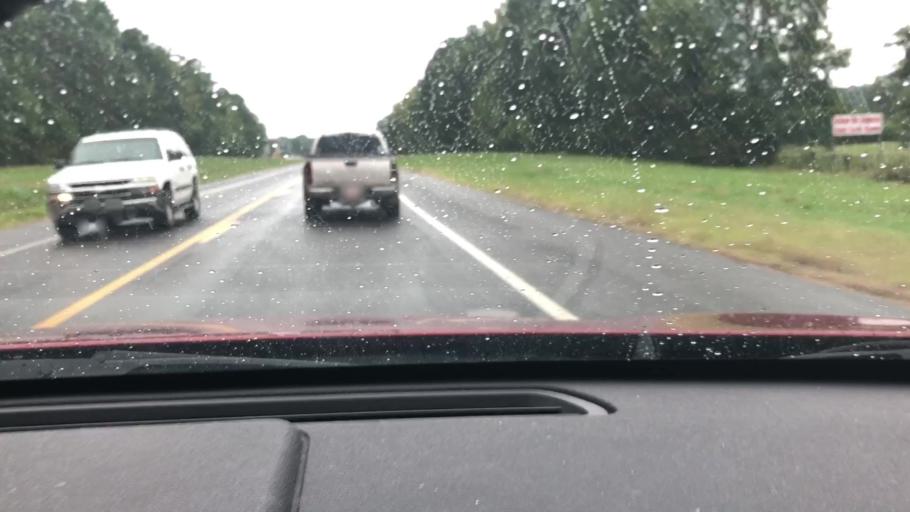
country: US
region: Arkansas
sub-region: Columbia County
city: Magnolia
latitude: 33.2968
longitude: -93.2446
